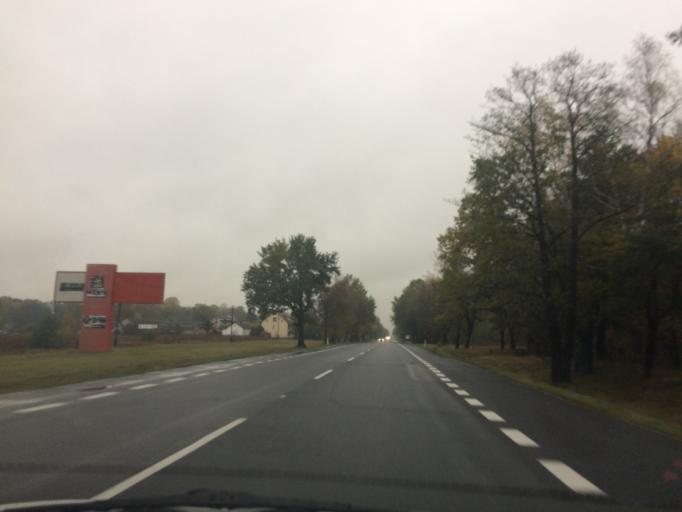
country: PL
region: Masovian Voivodeship
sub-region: Powiat otwocki
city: Celestynow
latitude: 52.0873
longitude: 21.4267
